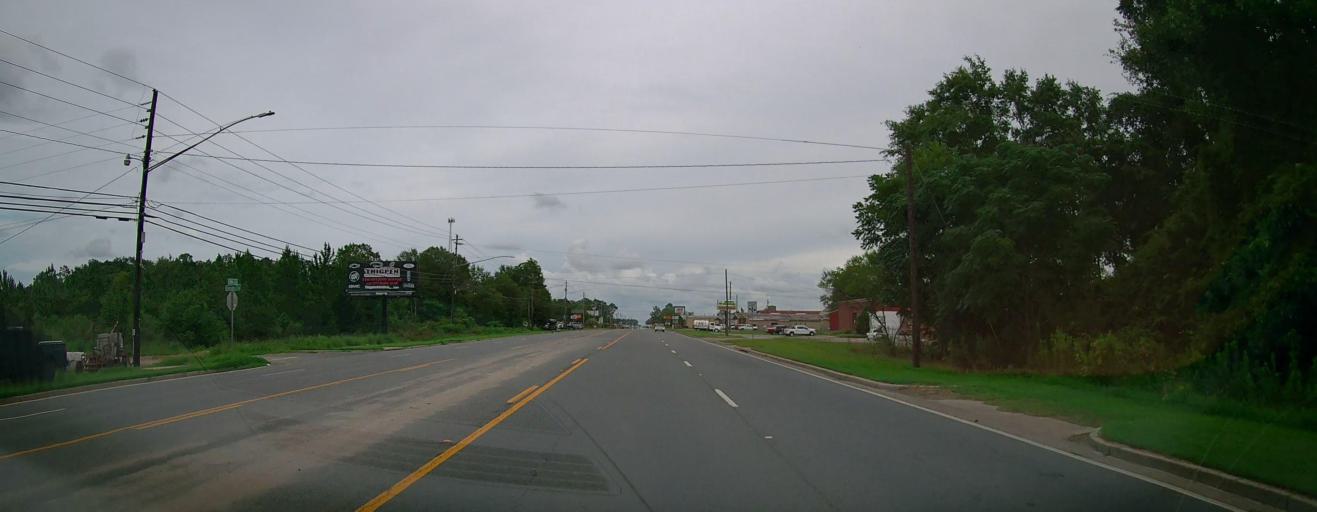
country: US
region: Georgia
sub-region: Appling County
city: Baxley
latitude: 31.7750
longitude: -82.3380
